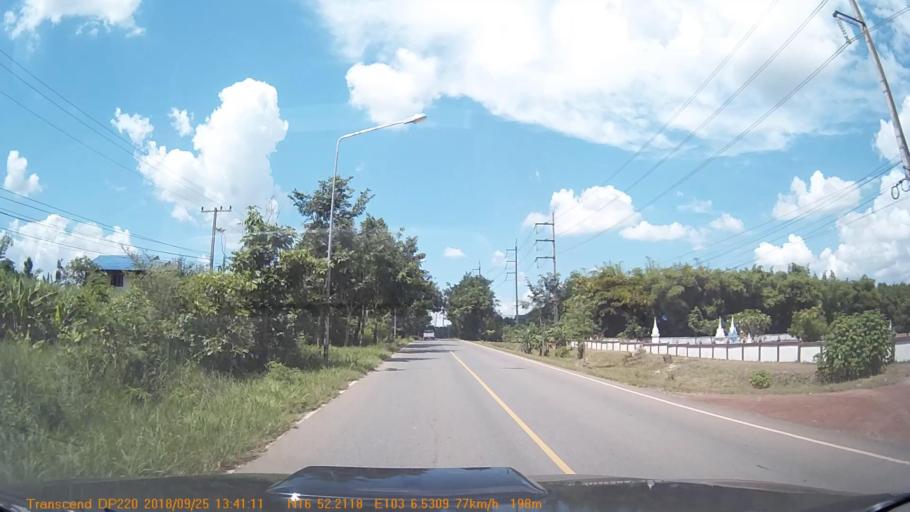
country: TH
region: Changwat Udon Thani
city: Si That
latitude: 16.8704
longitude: 103.1089
